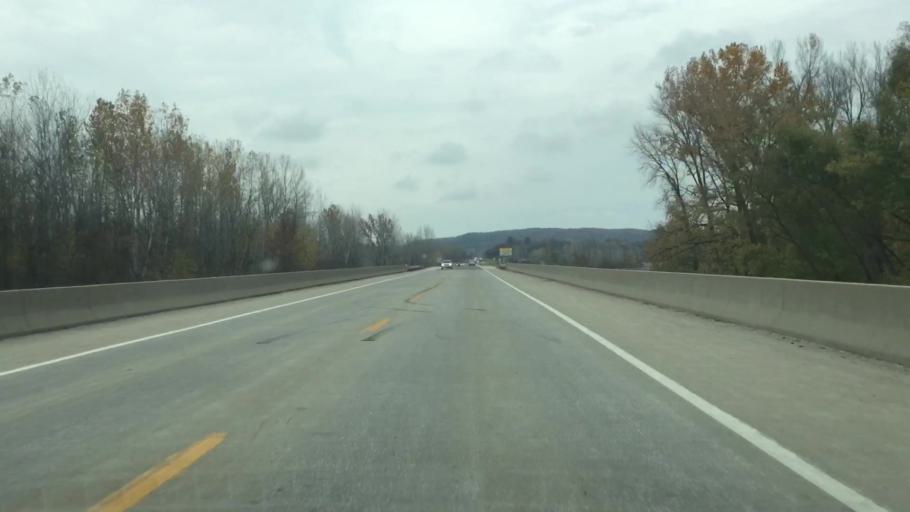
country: US
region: Missouri
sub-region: Gasconade County
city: Hermann
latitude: 38.7192
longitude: -91.4425
